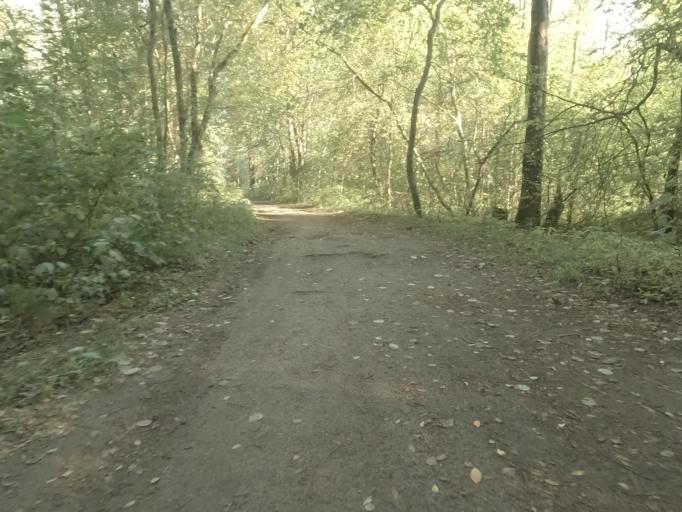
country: RU
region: Leningrad
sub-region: Volosovskiy Rayon
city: Shlissel'burg
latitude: 59.9459
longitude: 31.0044
